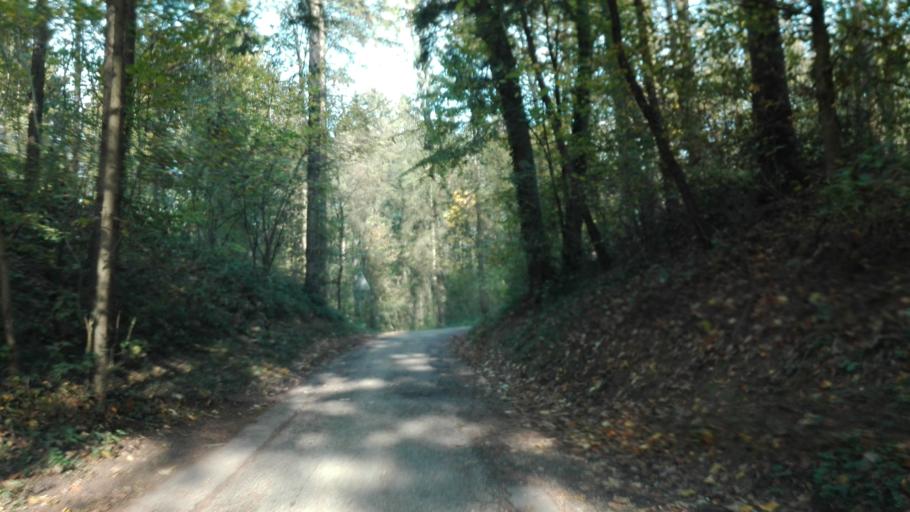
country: AT
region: Upper Austria
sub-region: Politischer Bezirk Perg
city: Perg
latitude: 48.2541
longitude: 14.6223
